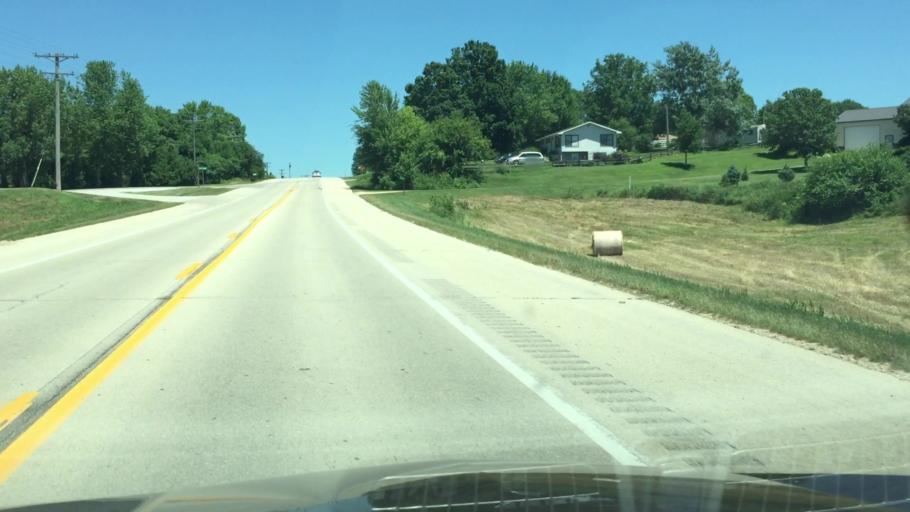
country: US
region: Iowa
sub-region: Jackson County
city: Maquoketa
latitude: 42.0644
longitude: -90.6909
